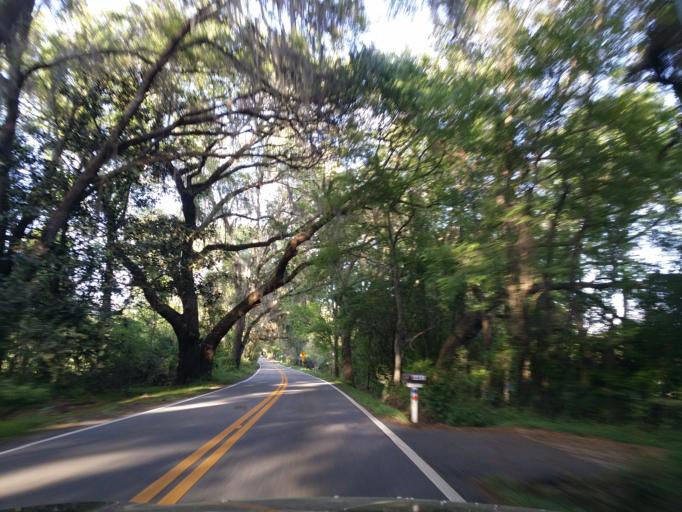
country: US
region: Florida
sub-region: Leon County
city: Tallahassee
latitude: 30.4830
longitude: -84.2014
